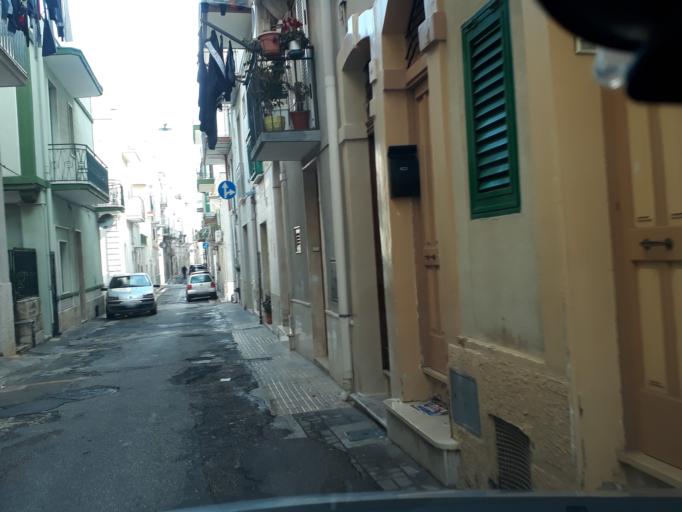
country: IT
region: Apulia
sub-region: Provincia di Brindisi
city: Fasano
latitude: 40.8339
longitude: 17.3560
